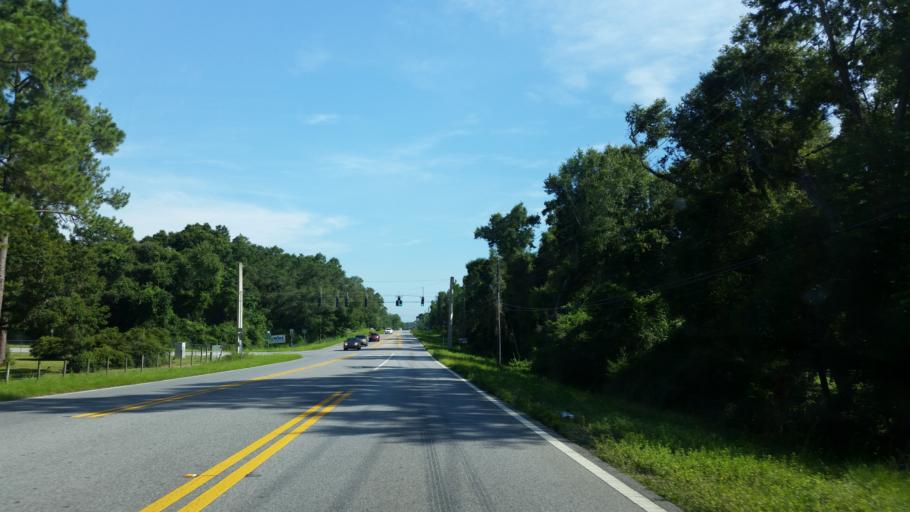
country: US
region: Florida
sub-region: Santa Rosa County
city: Pace
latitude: 30.6158
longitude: -87.1611
